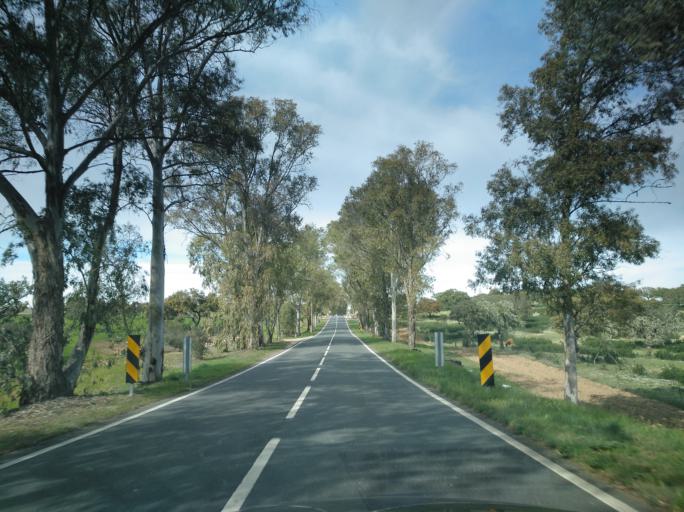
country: PT
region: Beja
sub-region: Mertola
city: Mertola
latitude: 37.7250
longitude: -7.7640
